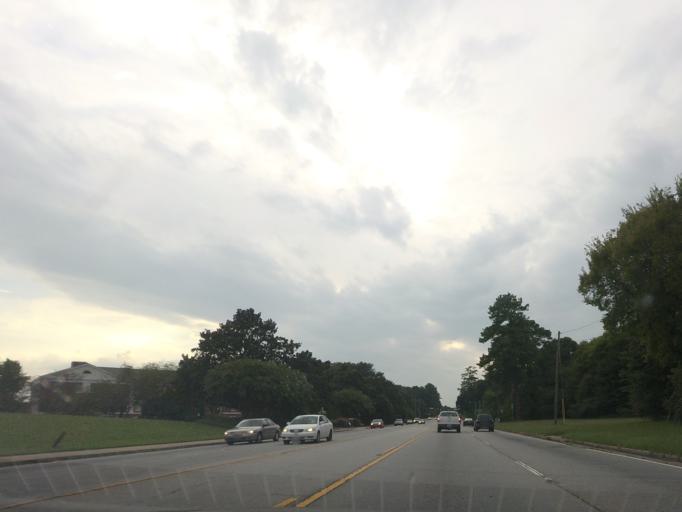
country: US
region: Georgia
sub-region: Bibb County
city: Macon
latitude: 32.8762
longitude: -83.7141
